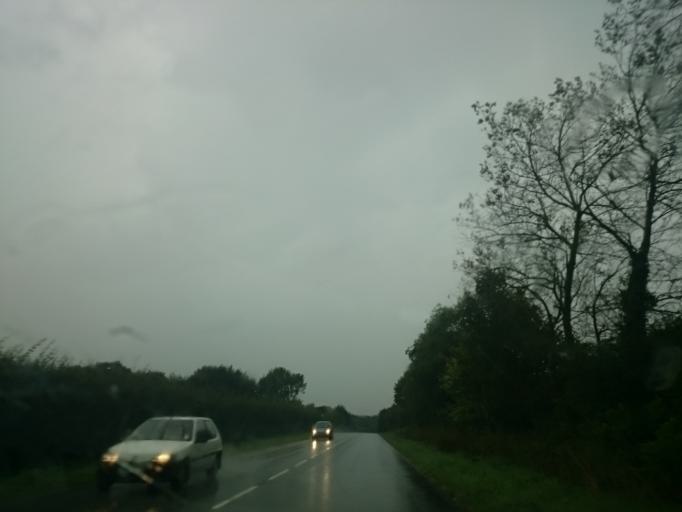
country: FR
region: Brittany
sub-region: Departement du Finistere
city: Plouvien
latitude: 48.5305
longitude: -4.4692
